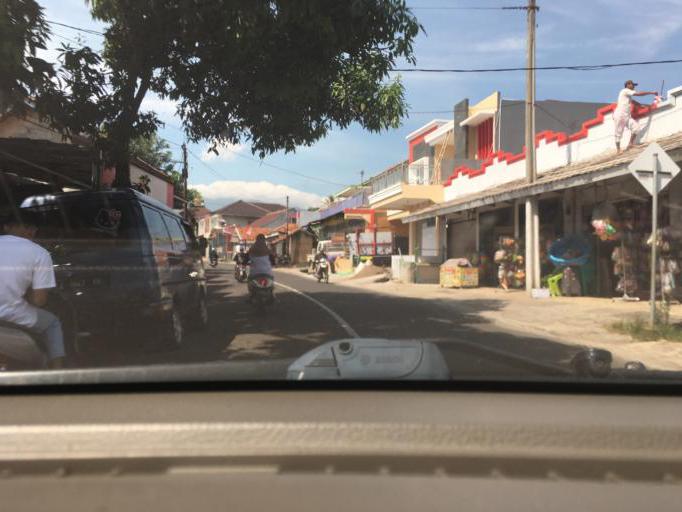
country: ID
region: West Java
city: Cilengkrang
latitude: -6.9483
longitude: 108.0923
